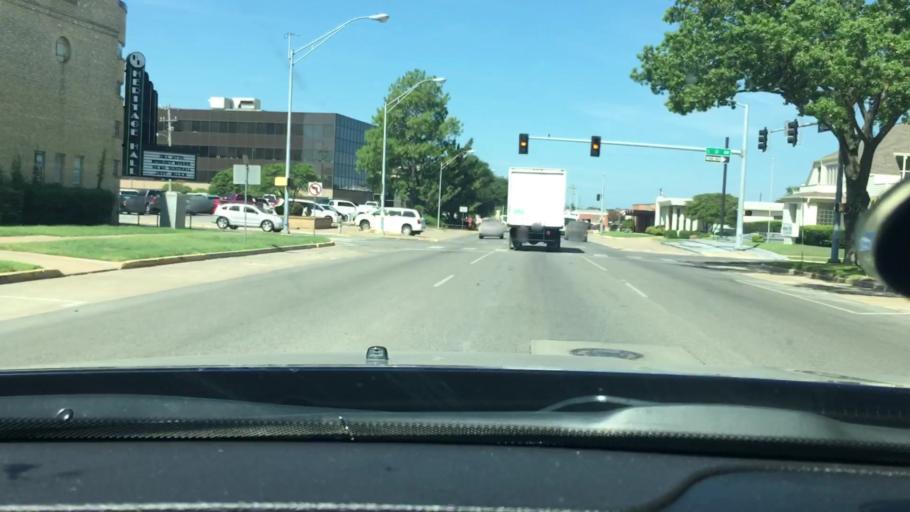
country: US
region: Oklahoma
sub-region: Carter County
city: Ardmore
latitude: 34.1744
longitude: -97.1309
